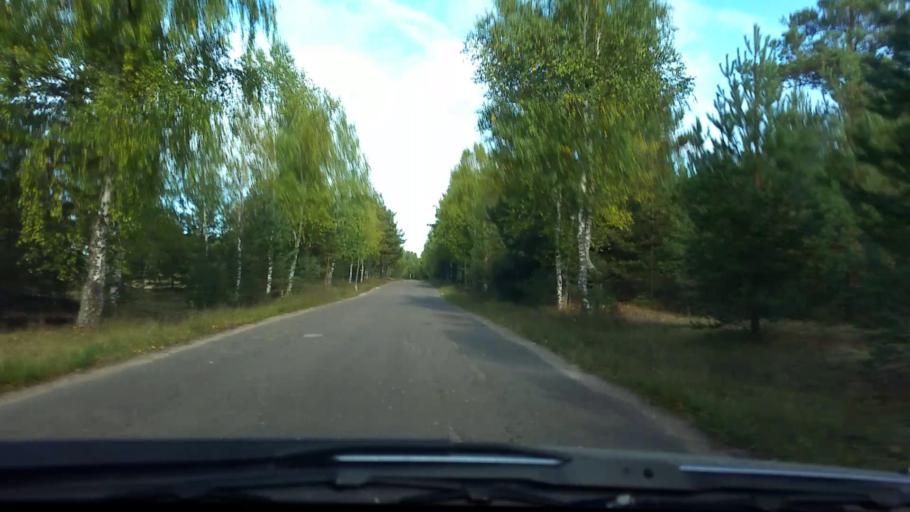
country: LV
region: Adazi
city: Adazi
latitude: 57.1107
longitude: 24.3641
